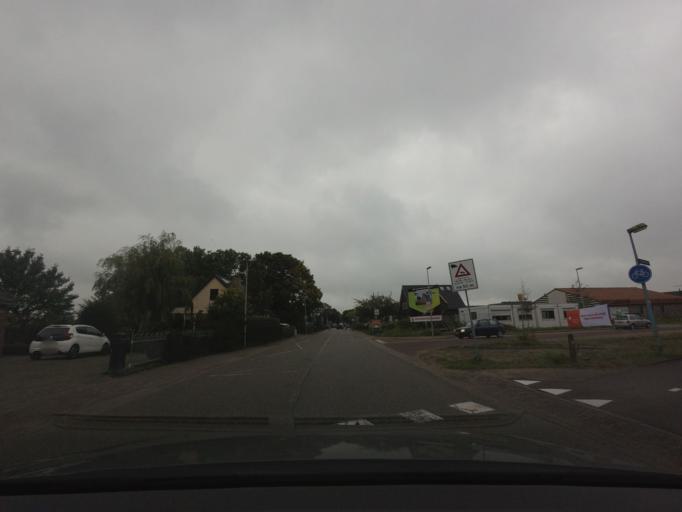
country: NL
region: North Holland
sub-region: Gemeente Alkmaar
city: Alkmaar
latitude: 52.6479
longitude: 4.7771
